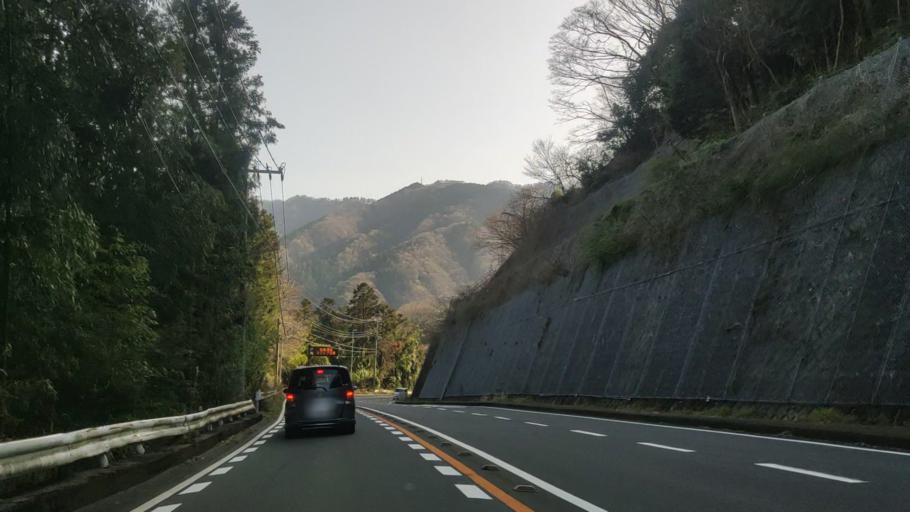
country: JP
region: Tokyo
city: Hachioji
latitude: 35.5479
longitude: 139.2633
